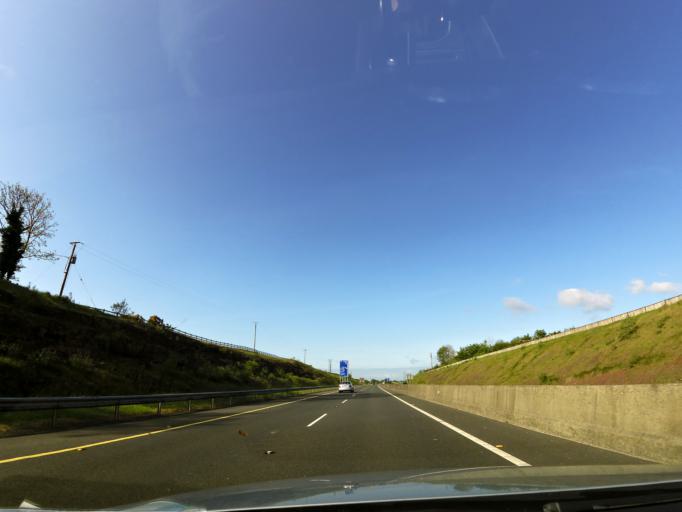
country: IE
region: Munster
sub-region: North Tipperary
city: Newport
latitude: 52.7644
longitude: -8.3934
